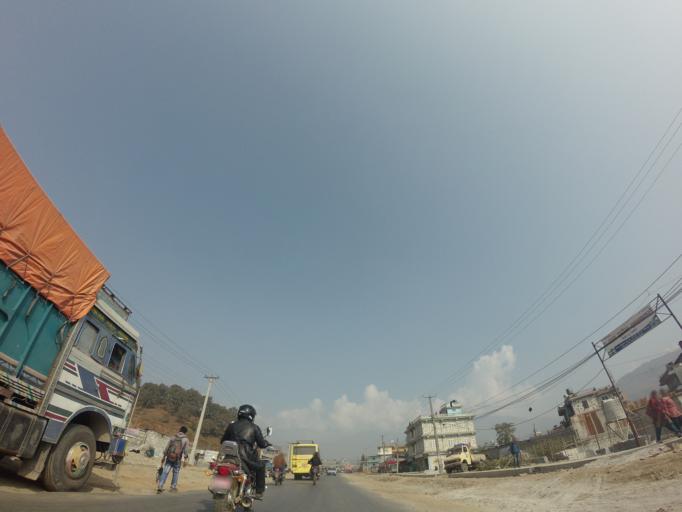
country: NP
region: Western Region
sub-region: Gandaki Zone
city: Pokhara
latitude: 28.2263
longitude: 83.9808
